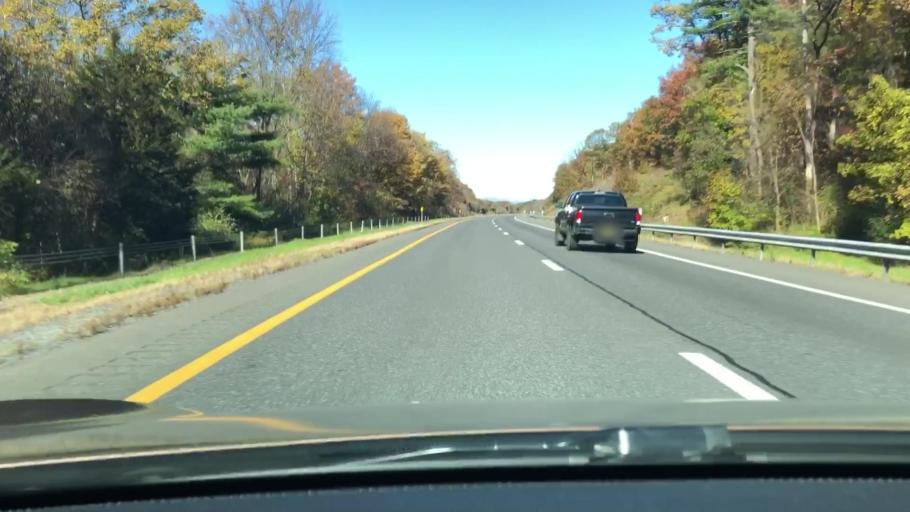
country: US
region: New York
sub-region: Ulster County
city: Tillson
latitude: 41.7952
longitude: -74.0515
